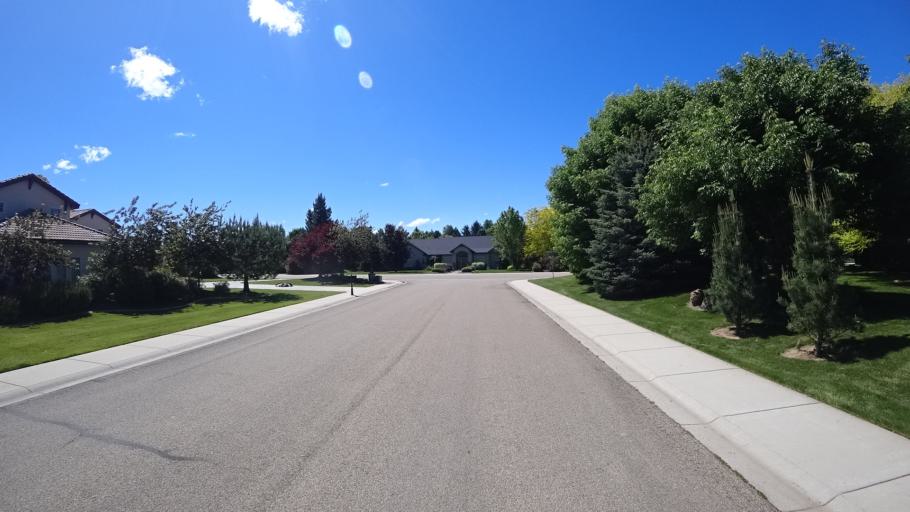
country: US
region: Idaho
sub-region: Ada County
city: Eagle
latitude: 43.6643
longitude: -116.3806
